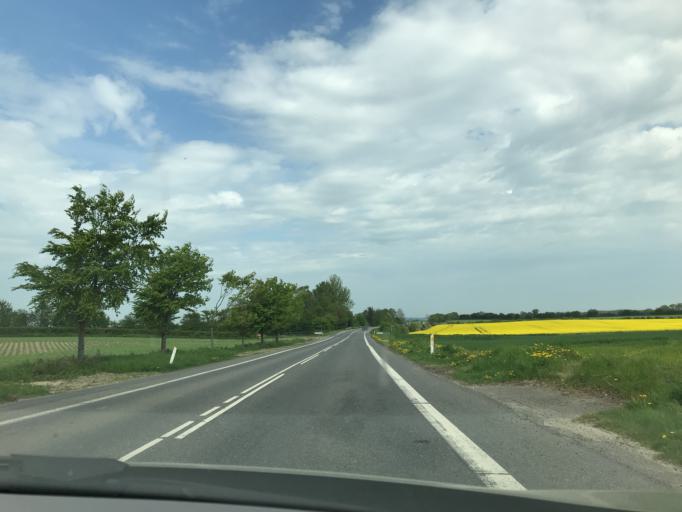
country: DK
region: South Denmark
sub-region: Assens Kommune
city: Assens
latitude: 55.2847
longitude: 9.9221
